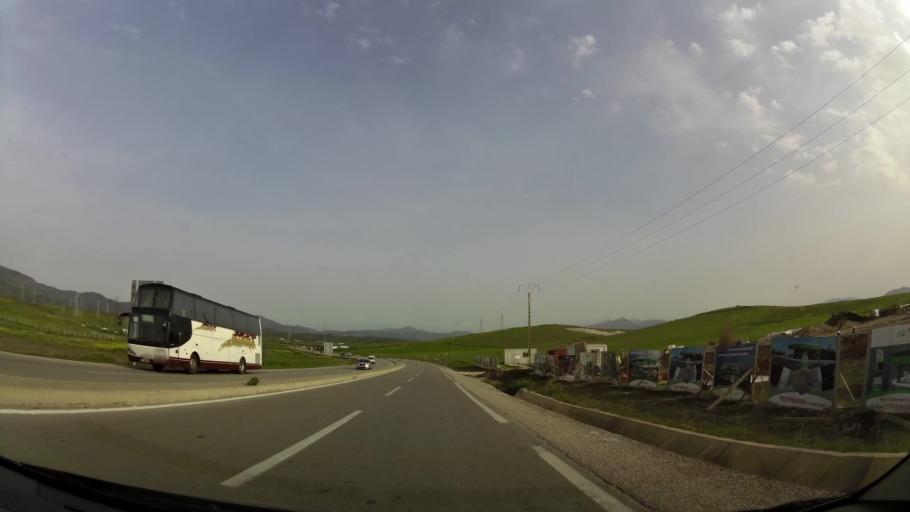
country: MA
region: Tanger-Tetouan
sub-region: Tanger-Assilah
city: Dar Chaoui
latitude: 35.6340
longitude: -5.6809
